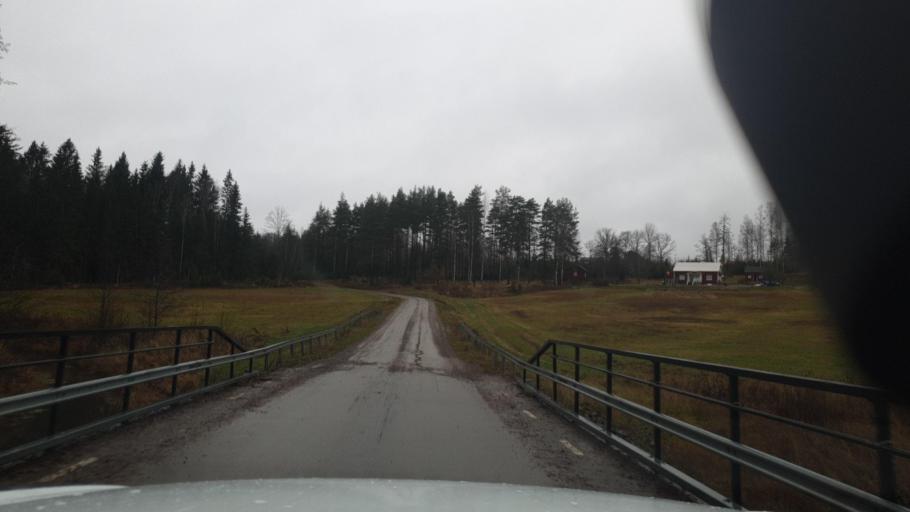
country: SE
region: Vaermland
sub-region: Arvika Kommun
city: Arvika
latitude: 59.5044
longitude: 12.7342
